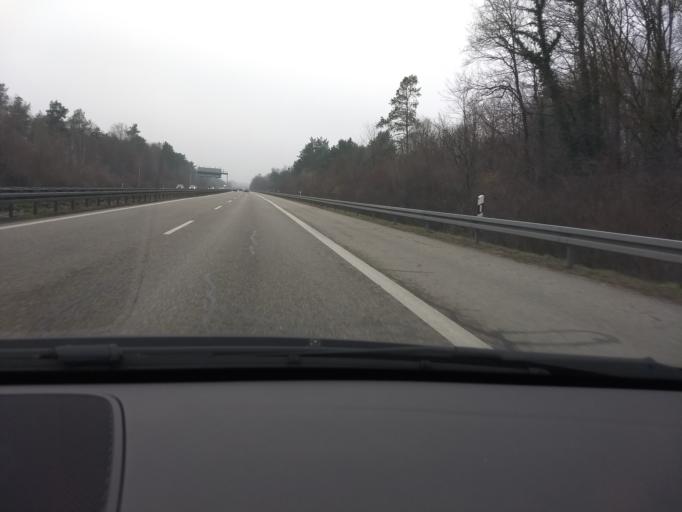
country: DE
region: Baden-Wuerttemberg
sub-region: Freiburg Region
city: Efringen-Kirchen
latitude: 47.6433
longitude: 7.5550
